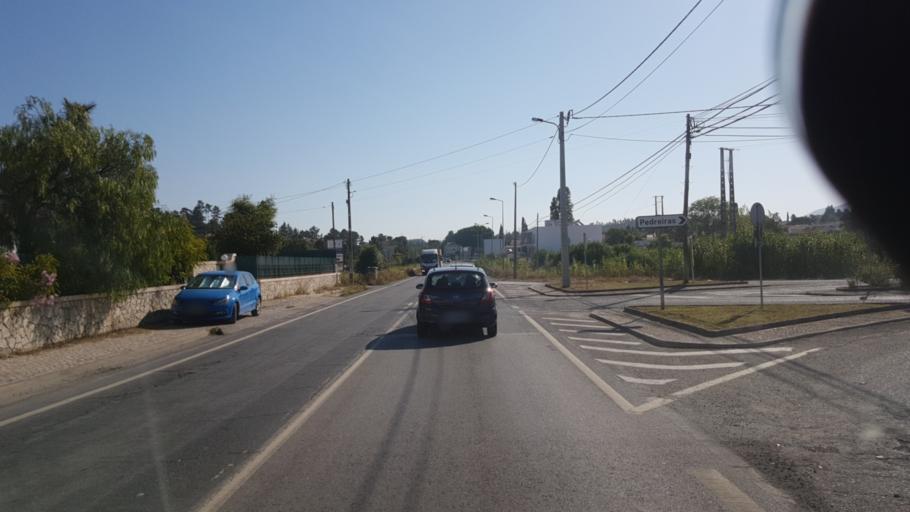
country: PT
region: Setubal
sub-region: Sesimbra
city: Sesimbra
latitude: 38.4745
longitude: -9.0802
